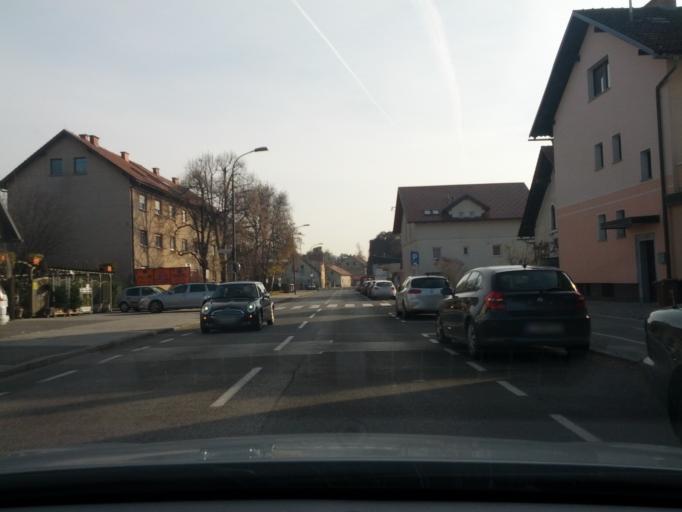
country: SI
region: Ljubljana
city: Ljubljana
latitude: 46.0693
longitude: 14.4824
